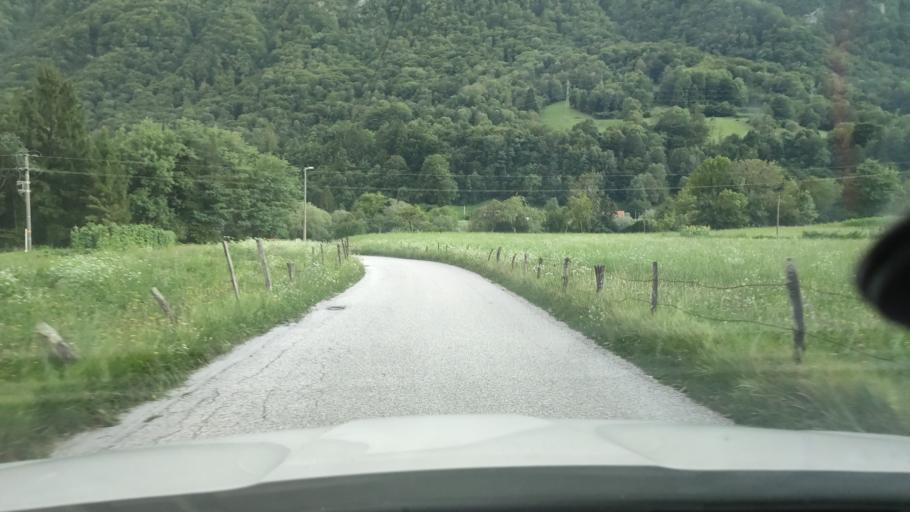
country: IT
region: Friuli Venezia Giulia
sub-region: Provincia di Udine
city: Cras
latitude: 46.2123
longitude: 13.6366
